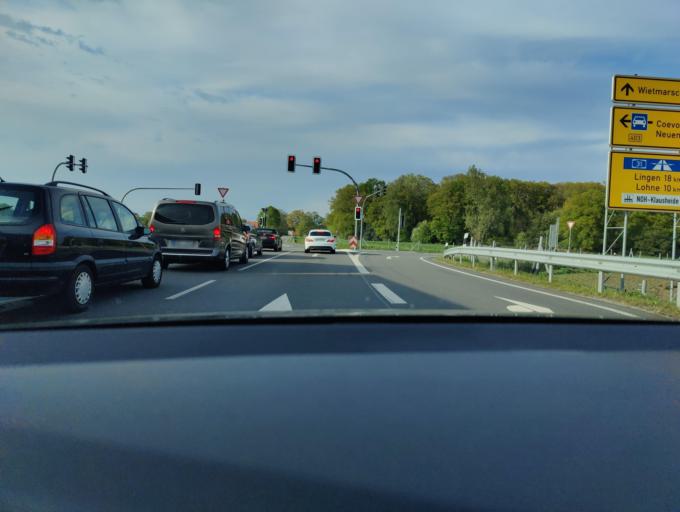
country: DE
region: Lower Saxony
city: Nordhorn
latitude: 52.4563
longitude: 7.0898
